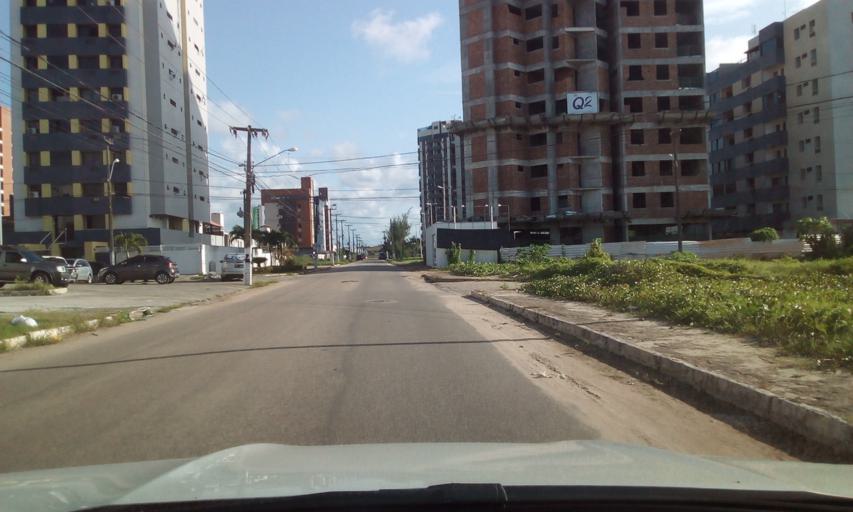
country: BR
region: Paraiba
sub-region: Cabedelo
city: Cabedelo
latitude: -7.0455
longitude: -34.8454
